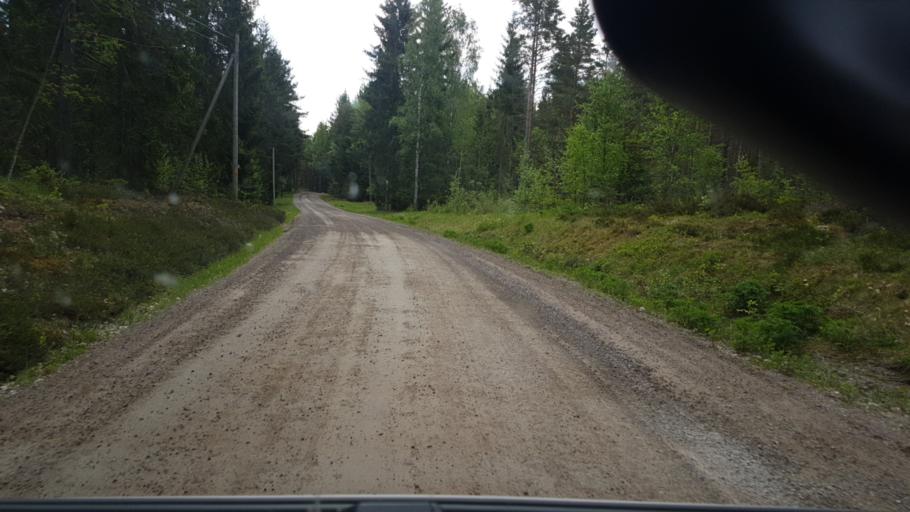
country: SE
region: Vaermland
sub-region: Arvika Kommun
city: Arvika
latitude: 59.5201
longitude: 12.7329
